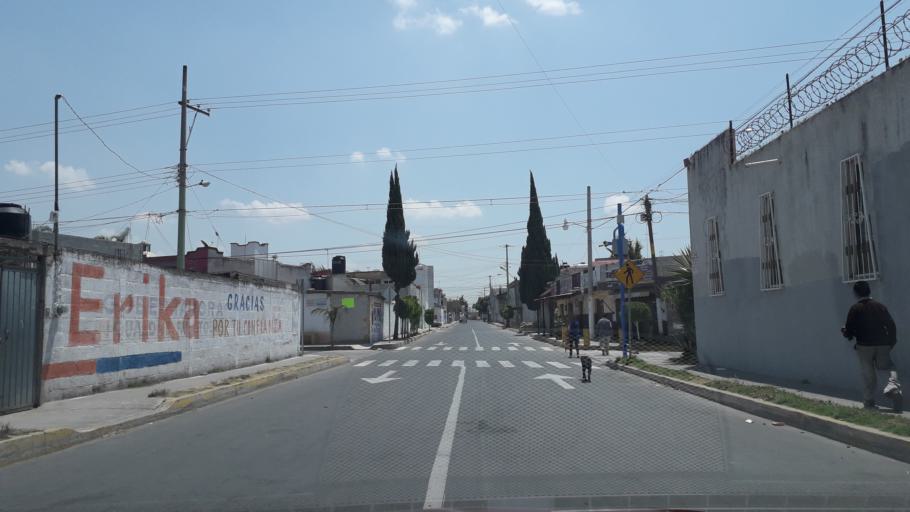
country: MX
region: Puebla
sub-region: Puebla
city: Primero de Mayo
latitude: 19.0697
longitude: -98.1213
